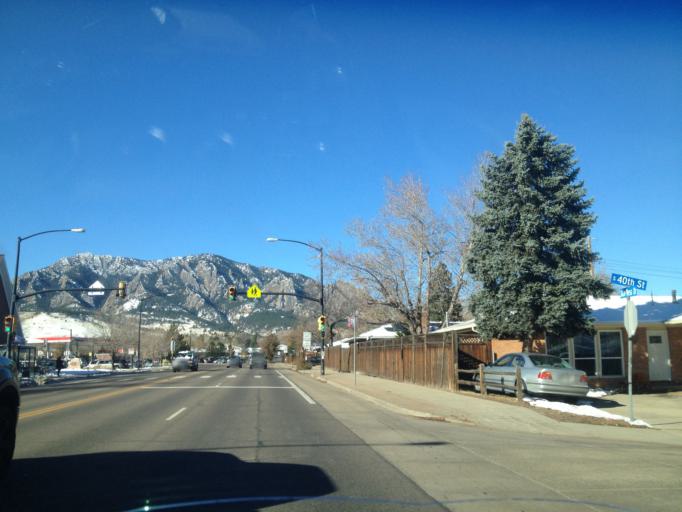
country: US
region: Colorado
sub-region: Boulder County
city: Boulder
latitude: 39.9859
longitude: -105.2472
